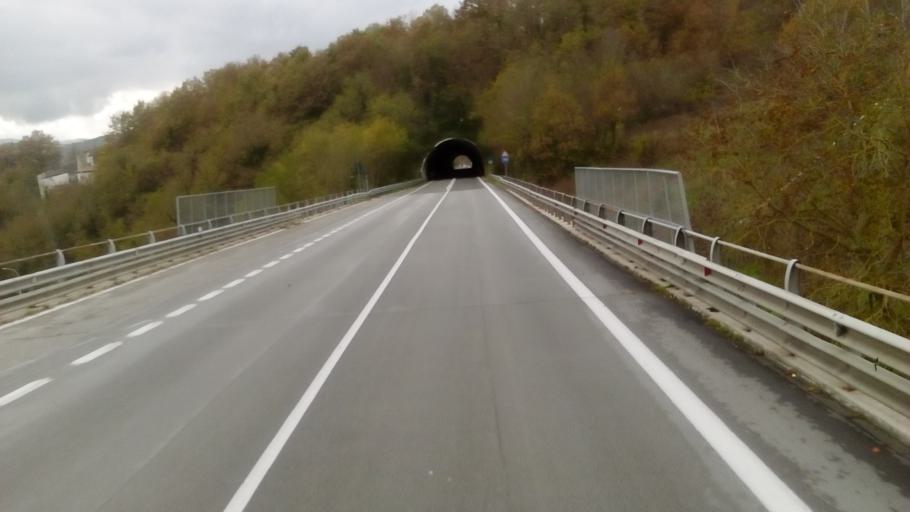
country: IT
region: Molise
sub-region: Provincia di Isernia
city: Sessano del Molise
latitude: 41.6416
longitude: 14.3255
